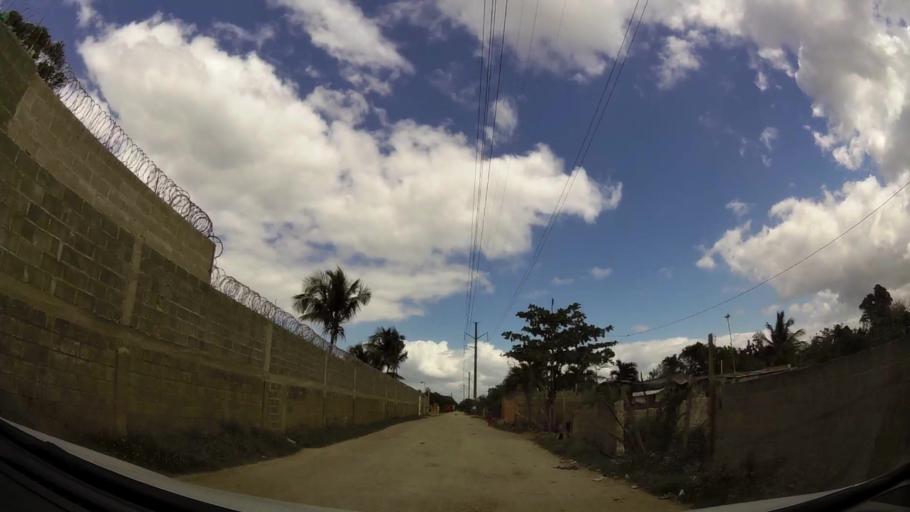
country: DO
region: Santo Domingo
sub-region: Santo Domingo
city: Boca Chica
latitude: 18.4522
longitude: -69.6484
